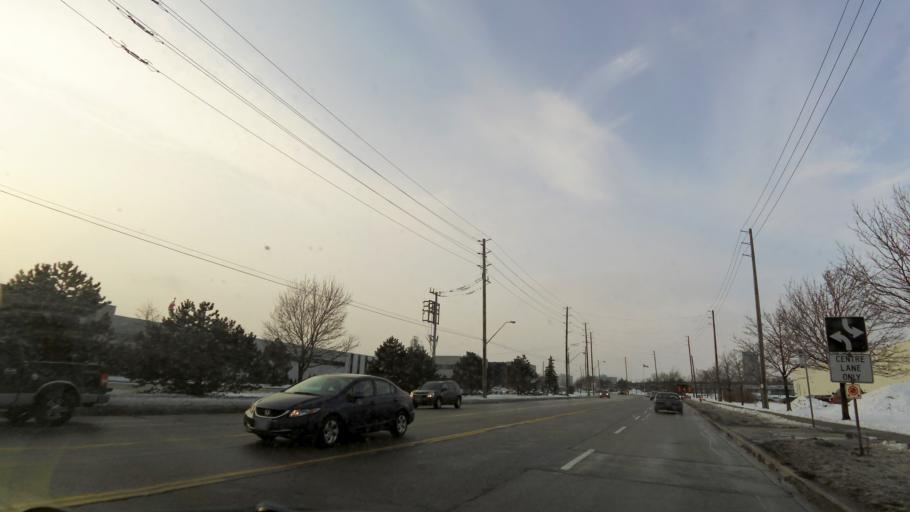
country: CA
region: Ontario
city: Brampton
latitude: 43.7025
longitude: -79.7229
